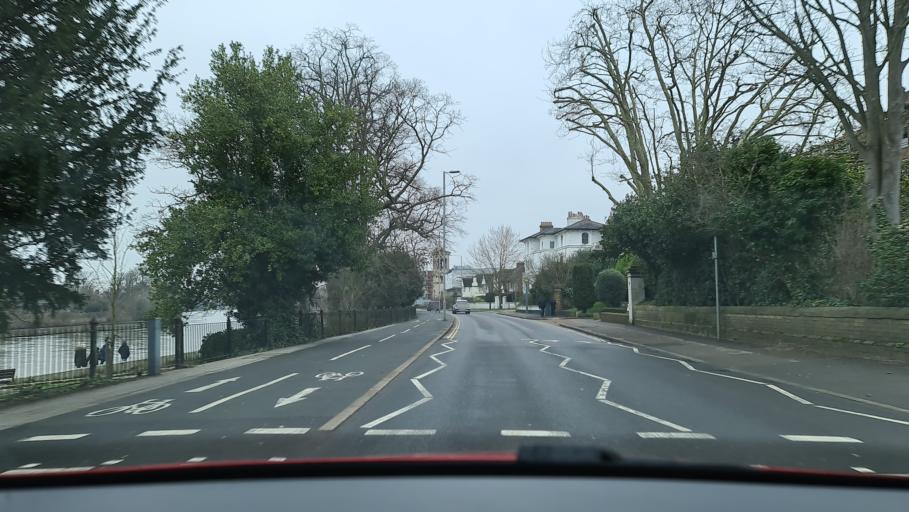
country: GB
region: England
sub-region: Greater London
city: Surbiton
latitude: 51.4000
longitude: -0.3087
